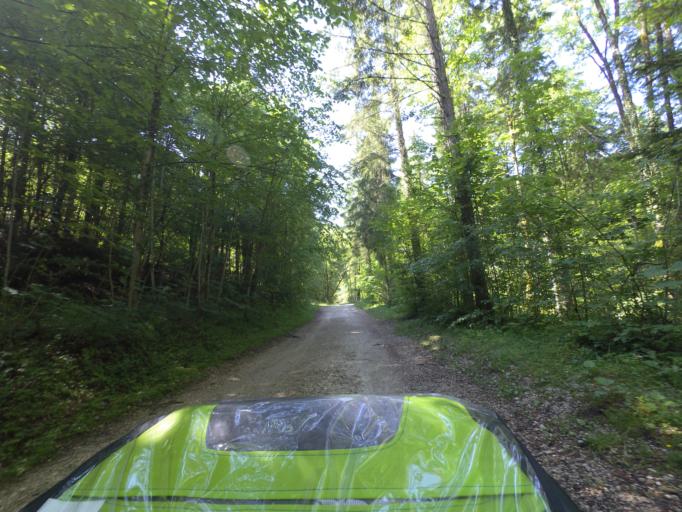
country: DE
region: Bavaria
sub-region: Upper Bavaria
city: Piding
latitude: 47.7340
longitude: 12.9467
